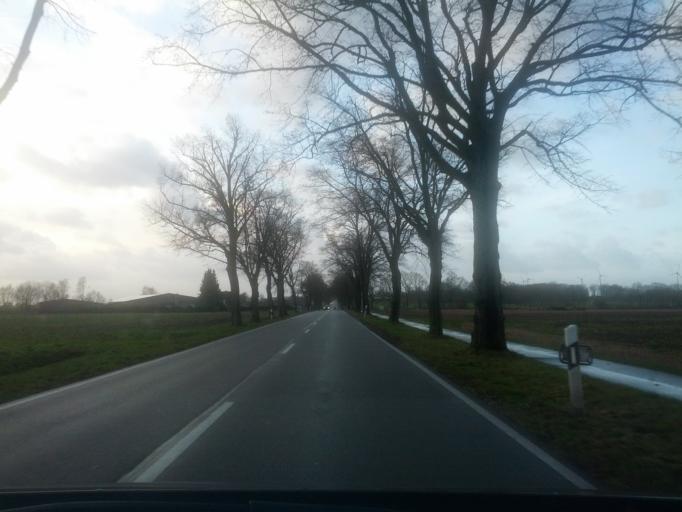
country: DE
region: Lower Saxony
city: Sittensen
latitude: 53.2653
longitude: 9.4944
